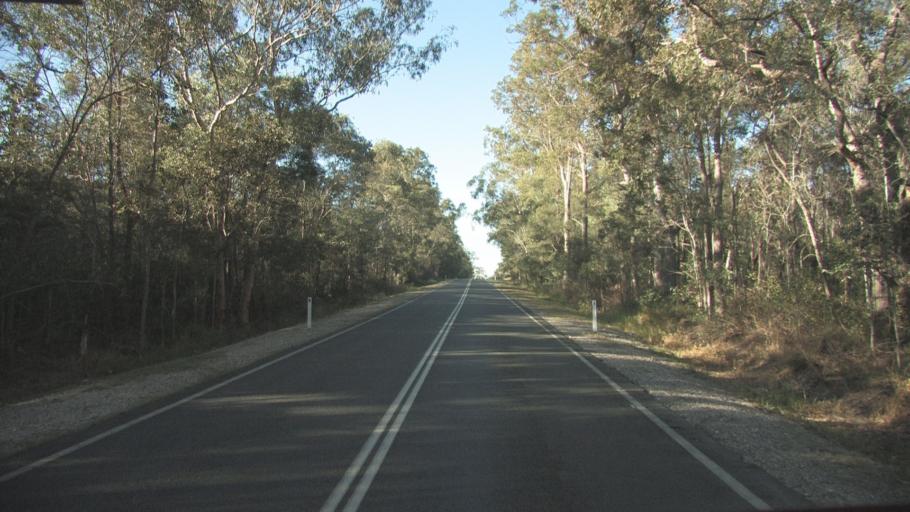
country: AU
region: Queensland
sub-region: Logan
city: Chambers Flat
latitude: -27.7785
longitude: 153.0732
